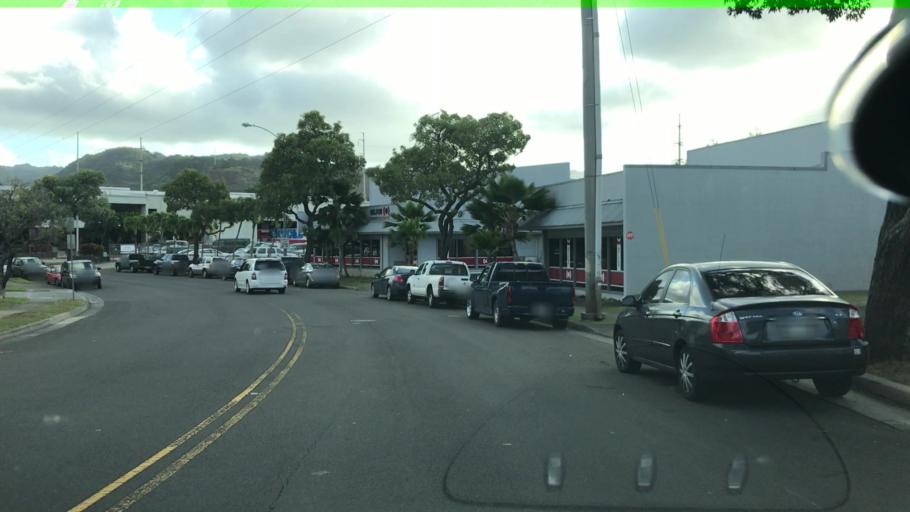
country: US
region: Hawaii
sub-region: Honolulu County
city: Halawa Heights
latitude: 21.3721
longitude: -157.9144
